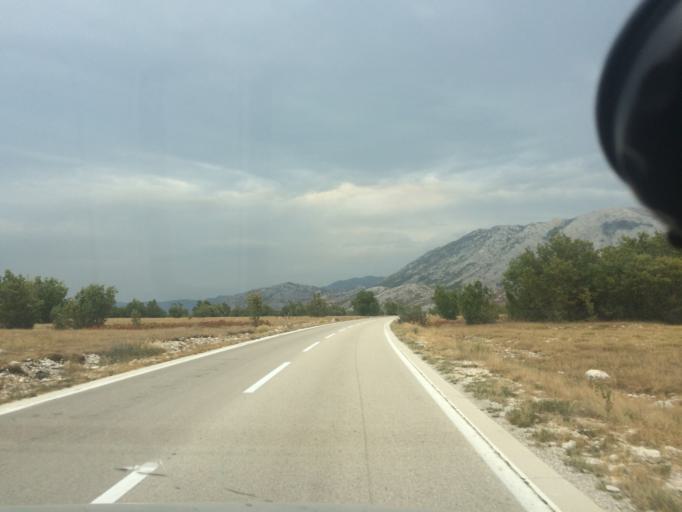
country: ME
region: Kotor
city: Risan
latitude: 42.5862
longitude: 18.6864
